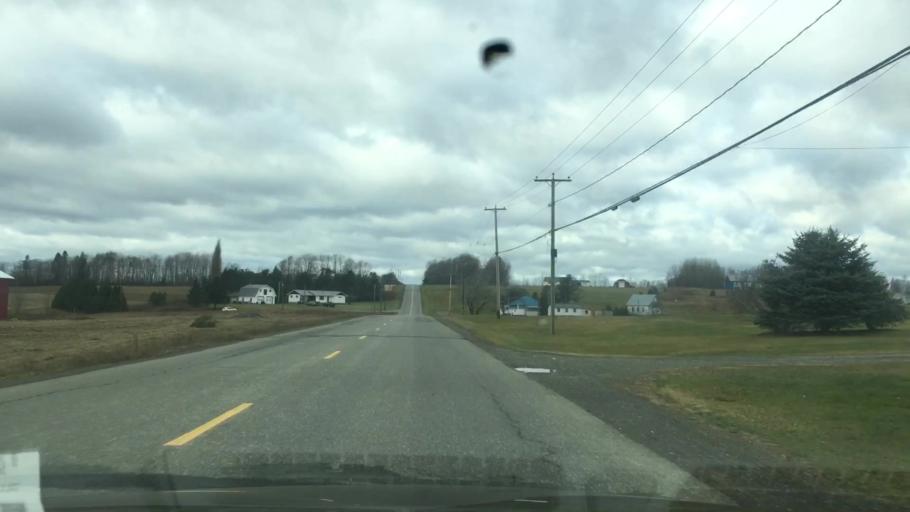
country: US
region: Maine
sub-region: Aroostook County
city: Fort Fairfield
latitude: 46.7583
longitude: -67.7691
